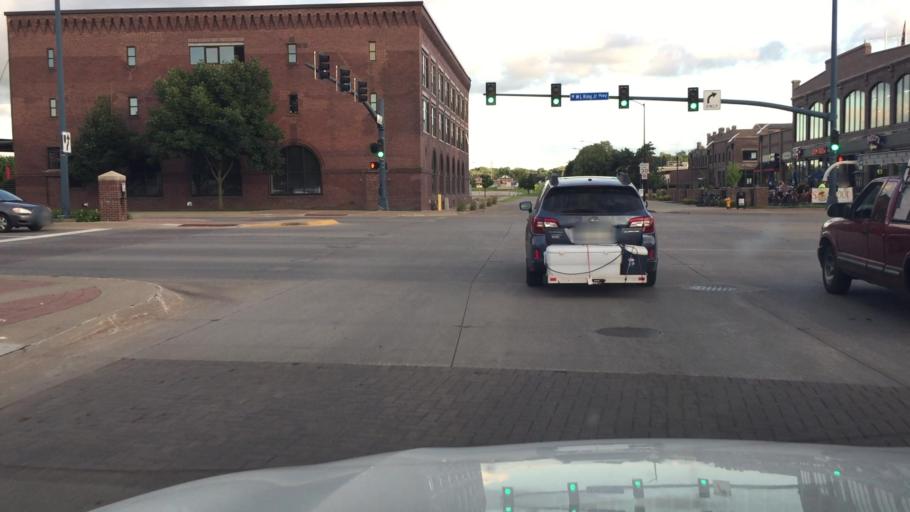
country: US
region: Iowa
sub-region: Polk County
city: Des Moines
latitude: 41.5825
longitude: -93.6194
